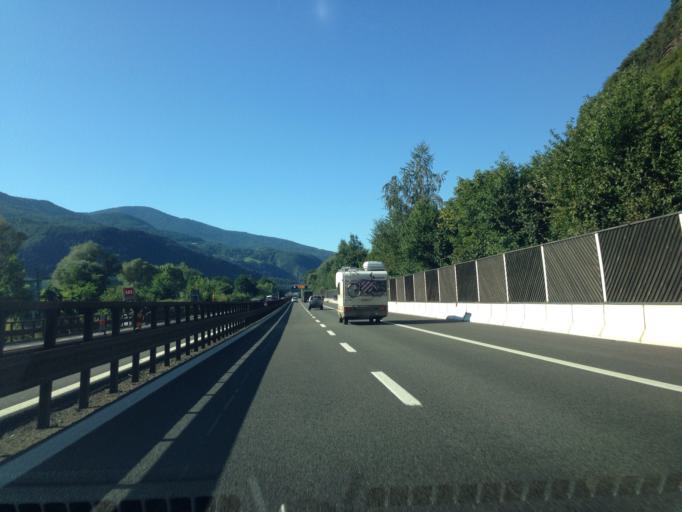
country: IT
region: Trentino-Alto Adige
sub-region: Bolzano
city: Bressanone
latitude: 46.6992
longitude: 11.6451
